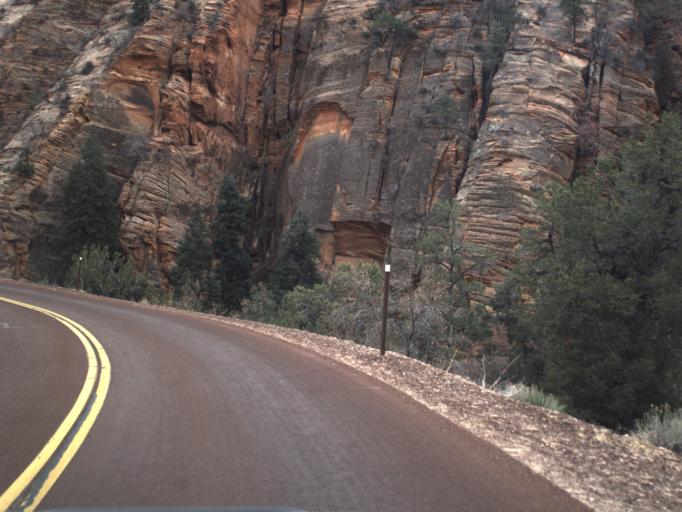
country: US
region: Utah
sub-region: Washington County
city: Hildale
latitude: 37.2160
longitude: -112.9198
